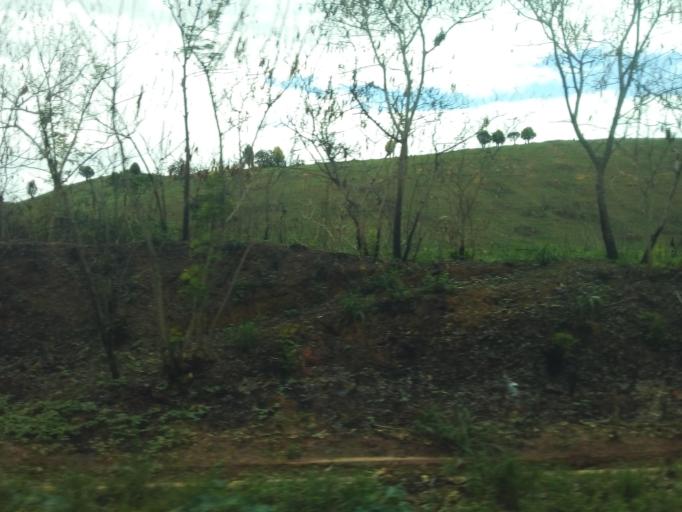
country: BR
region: Minas Gerais
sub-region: Governador Valadares
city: Governador Valadares
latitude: -19.0669
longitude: -42.1502
